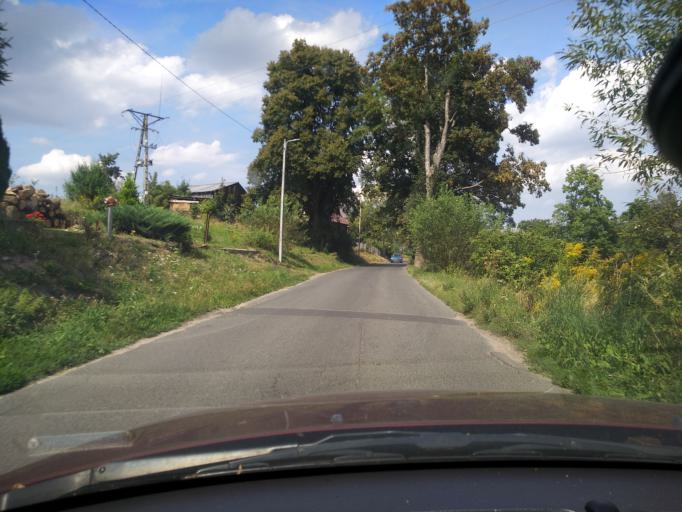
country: PL
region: Lower Silesian Voivodeship
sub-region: Powiat jeleniogorski
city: Stara Kamienica
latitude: 50.9094
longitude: 15.5691
